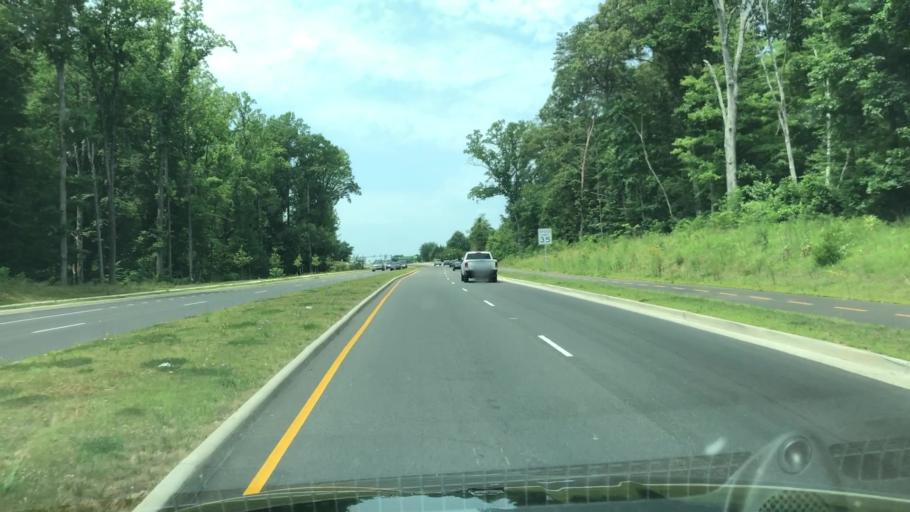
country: US
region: Virginia
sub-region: Stafford County
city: Falmouth
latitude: 38.3158
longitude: -77.4923
